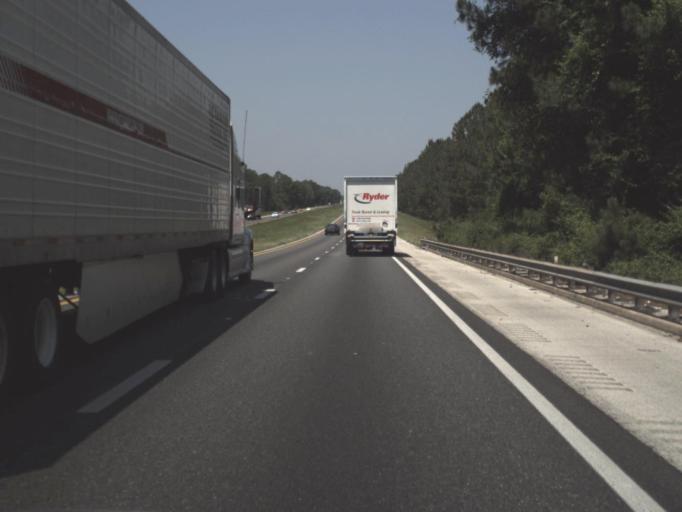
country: US
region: Florida
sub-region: Duval County
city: Baldwin
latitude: 30.3043
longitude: -81.9014
